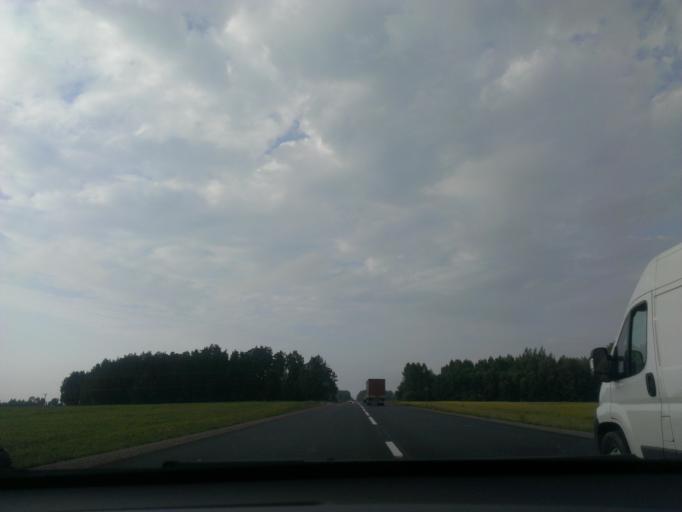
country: LV
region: Lecava
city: Iecava
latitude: 56.6504
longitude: 24.2293
